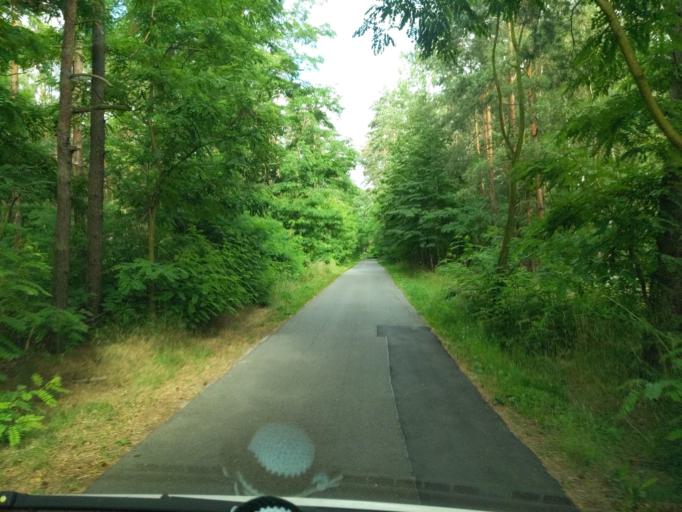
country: DE
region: Brandenburg
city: Cottbus
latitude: 51.6862
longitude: 14.3231
